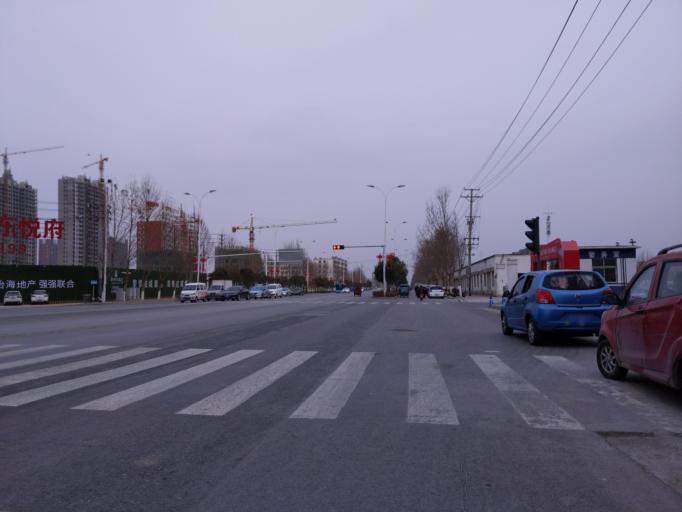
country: CN
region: Henan Sheng
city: Zhongyuanlu
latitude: 35.7572
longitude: 115.0770
